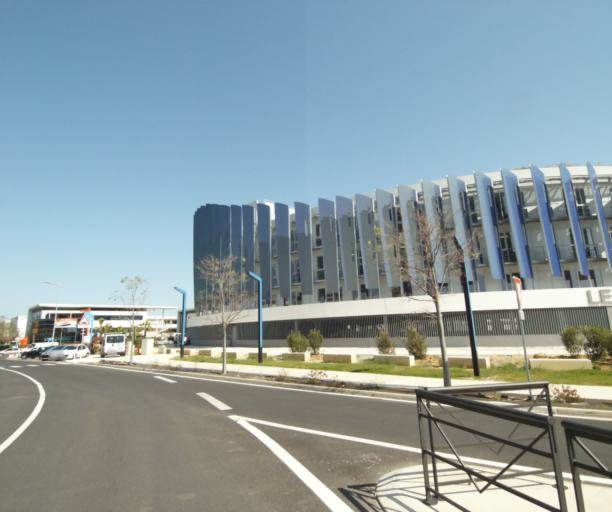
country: FR
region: Languedoc-Roussillon
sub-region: Departement de l'Herault
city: Perols
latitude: 43.5791
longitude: 3.9397
